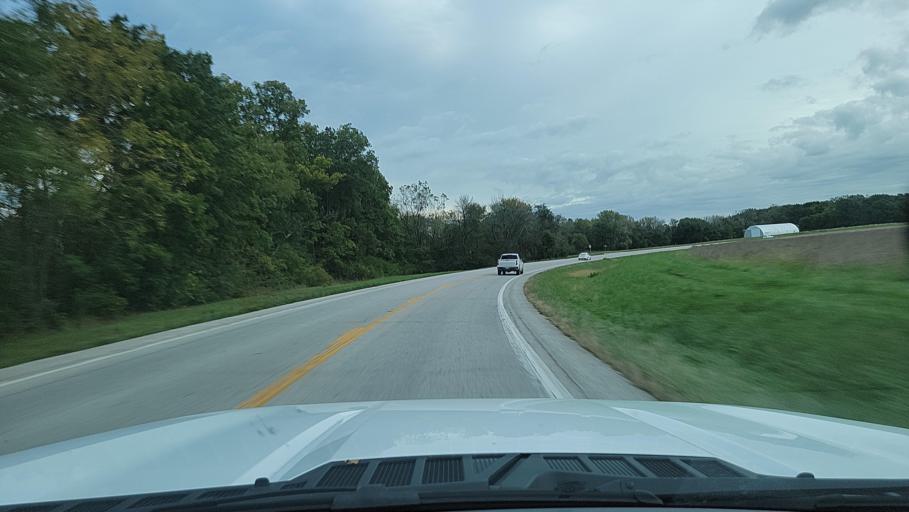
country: US
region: Illinois
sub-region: Schuyler County
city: Rushville
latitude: 40.1516
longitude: -90.5554
